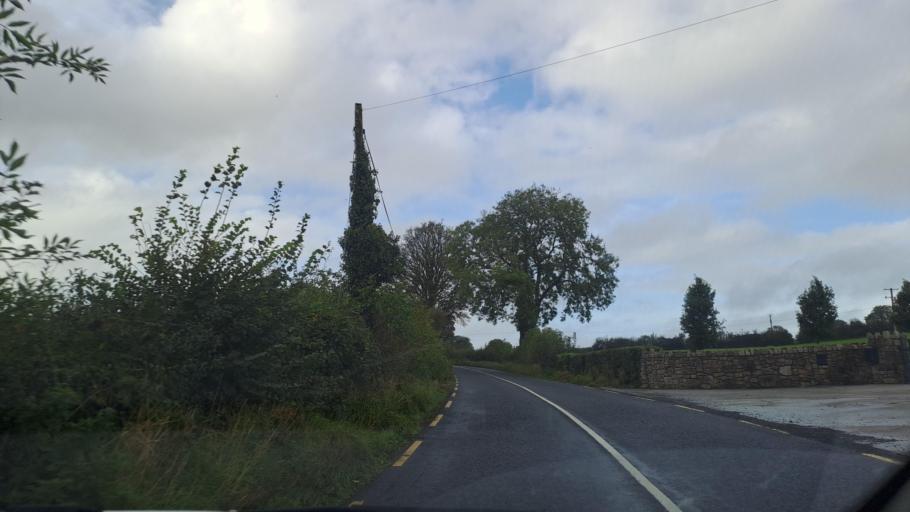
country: IE
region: Ulster
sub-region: County Monaghan
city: Carrickmacross
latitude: 53.9167
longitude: -6.7091
